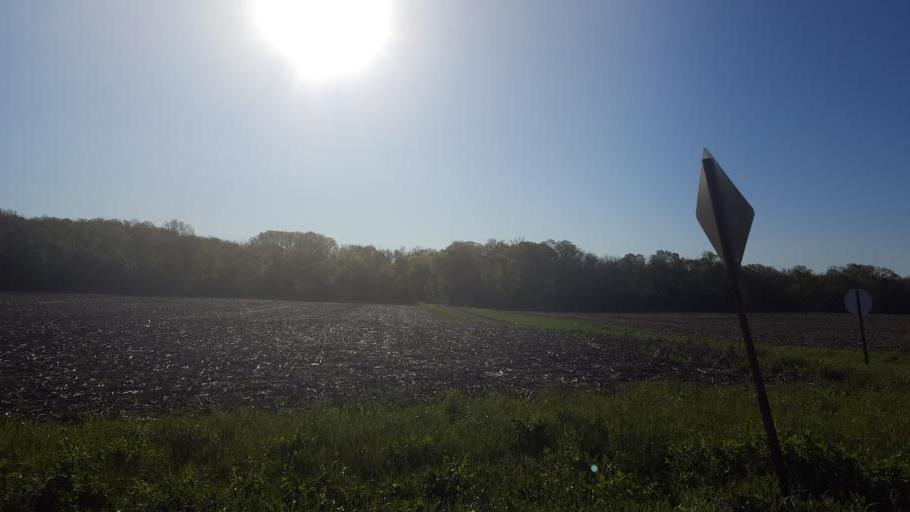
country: US
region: Ohio
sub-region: Delaware County
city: Sunbury
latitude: 40.3741
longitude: -82.8160
